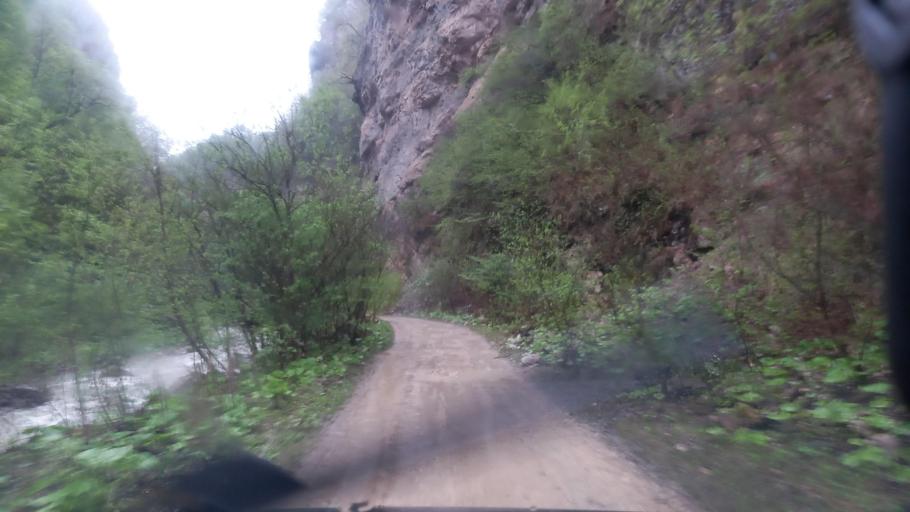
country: RU
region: Kabardino-Balkariya
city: Bylym
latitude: 43.5855
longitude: 43.0109
